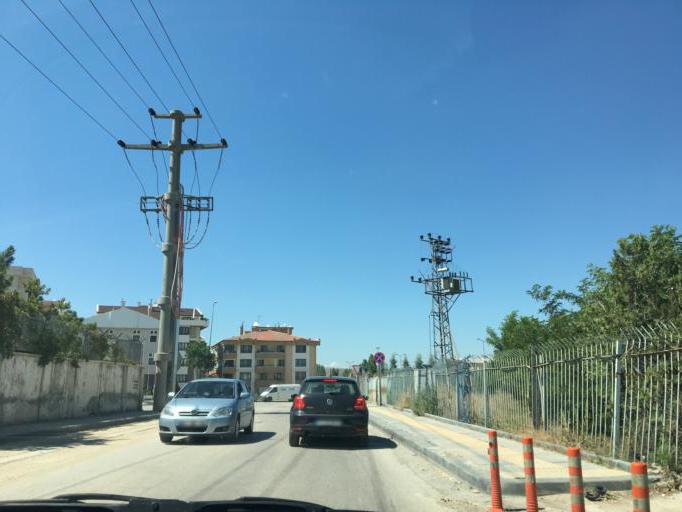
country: TR
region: Ankara
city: Batikent
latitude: 39.9109
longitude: 32.7748
